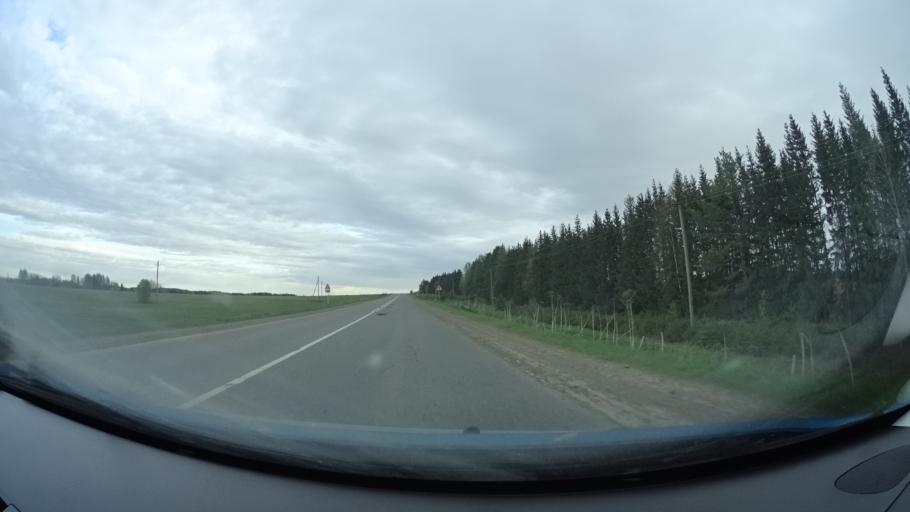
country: RU
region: Perm
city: Osa
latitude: 57.2722
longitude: 55.5703
